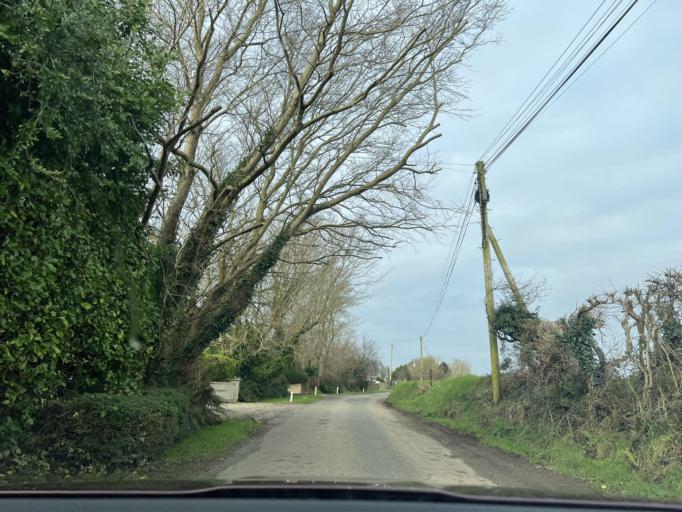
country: IE
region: Leinster
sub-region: Loch Garman
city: Loch Garman
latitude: 52.3639
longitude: -6.5287
